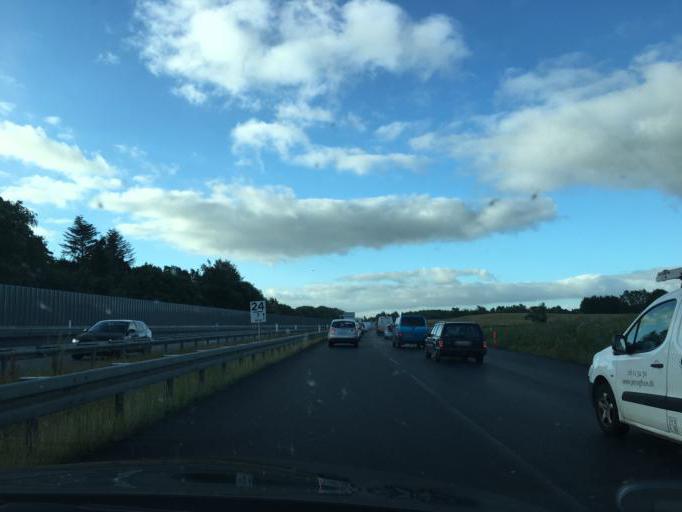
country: DK
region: Capital Region
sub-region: Horsholm Kommune
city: Horsholm
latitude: 55.8574
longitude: 12.4960
